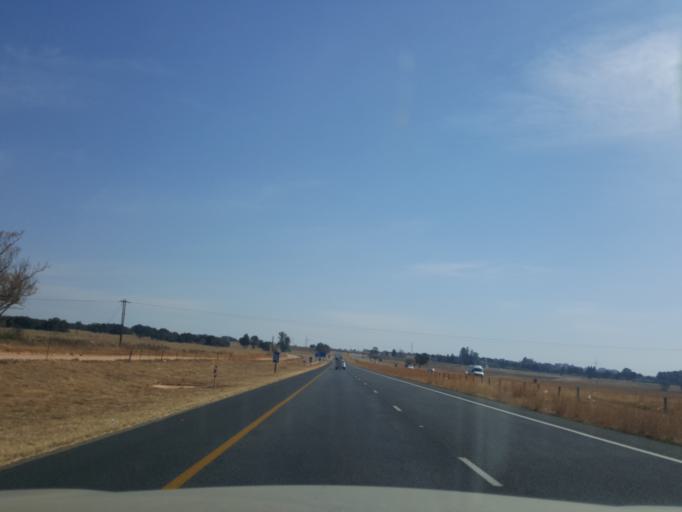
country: ZA
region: Gauteng
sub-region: City of Tshwane Metropolitan Municipality
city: Cullinan
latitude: -25.7977
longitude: 28.5272
